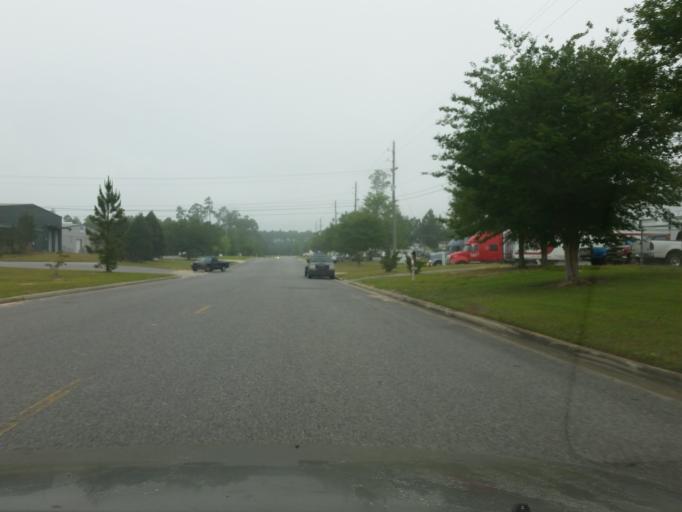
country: US
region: Florida
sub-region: Escambia County
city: Ferry Pass
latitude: 30.5201
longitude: -87.1909
